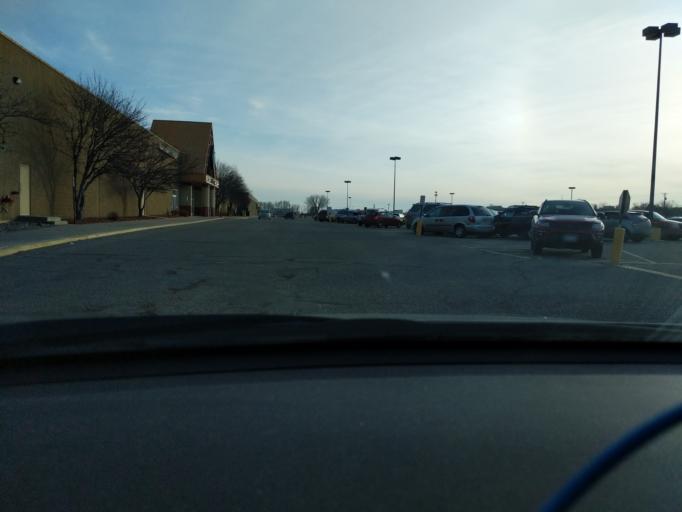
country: US
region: Minnesota
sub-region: Kandiyohi County
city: Willmar
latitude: 45.1069
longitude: -95.0408
